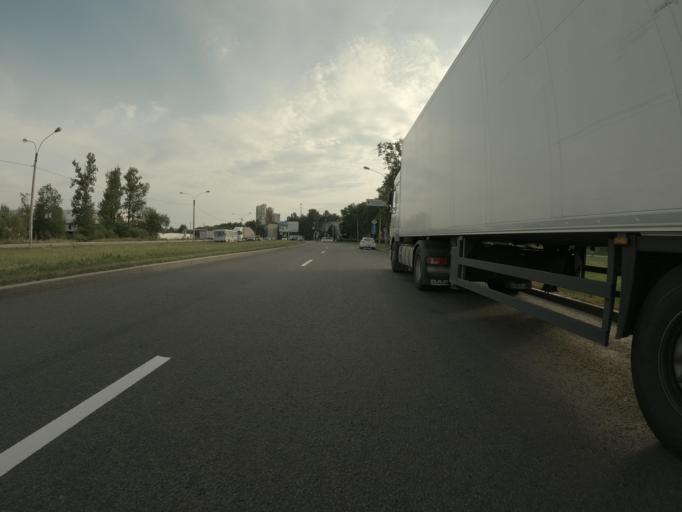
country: RU
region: Leningrad
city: Rybatskoye
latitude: 59.8788
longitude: 30.4816
